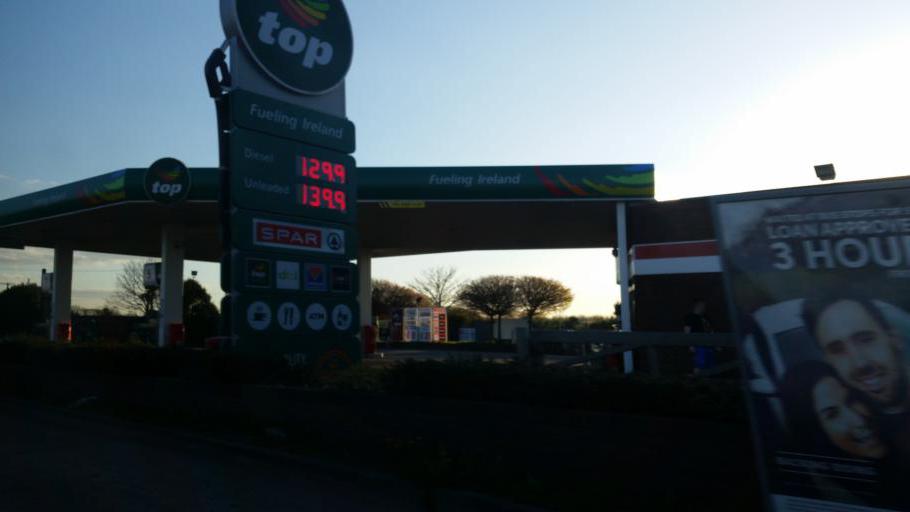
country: IE
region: Leinster
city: Lusk
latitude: 53.5011
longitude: -6.1938
